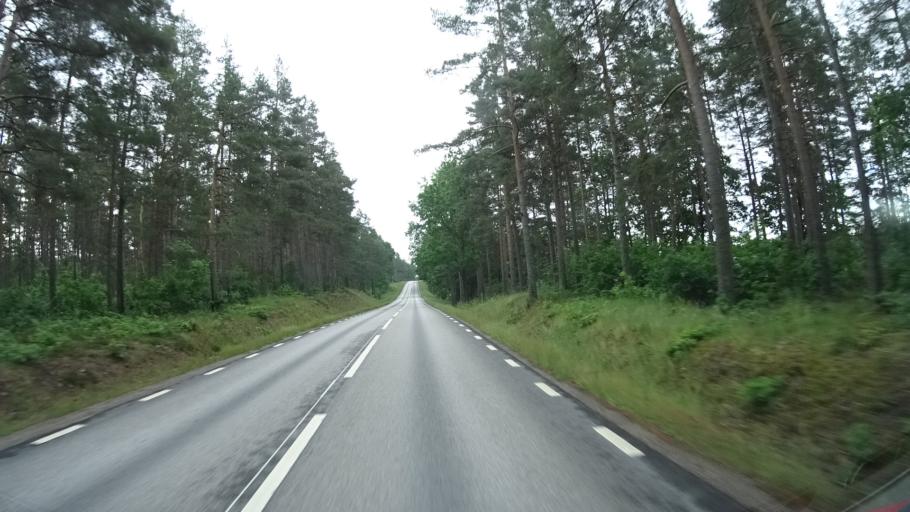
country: SE
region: Kalmar
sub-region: Oskarshamns Kommun
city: Oskarshamn
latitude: 57.3081
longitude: 16.2840
